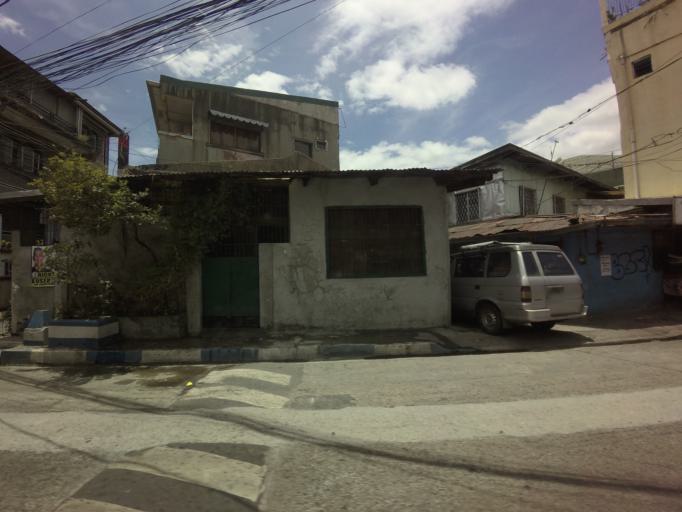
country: PH
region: Calabarzon
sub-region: Province of Rizal
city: Cainta
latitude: 14.5870
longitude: 121.0970
